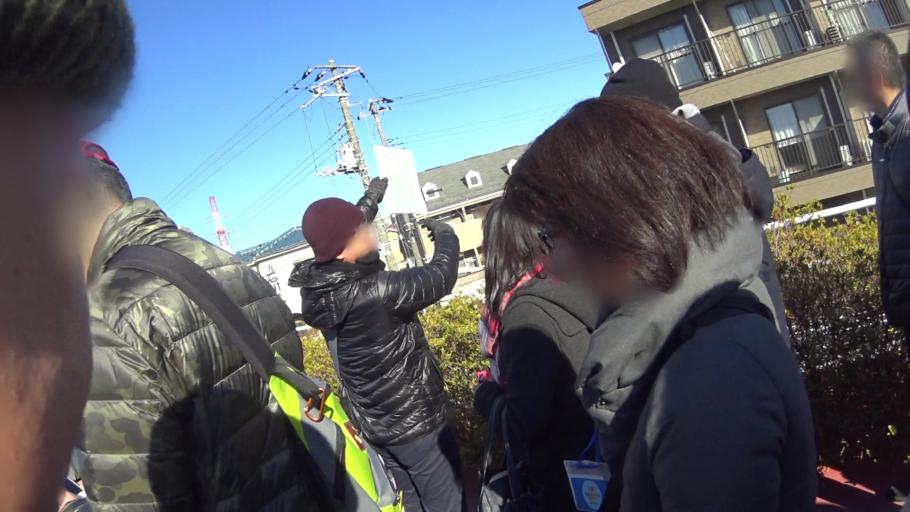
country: JP
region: Tokyo
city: Urayasu
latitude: 35.6453
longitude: 139.8857
